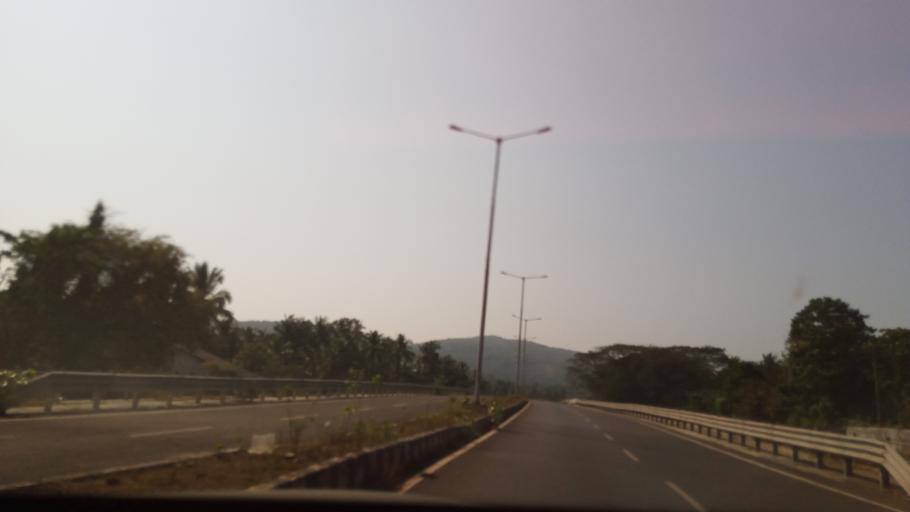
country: IN
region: Goa
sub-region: North Goa
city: Curti
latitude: 15.4210
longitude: 74.0532
